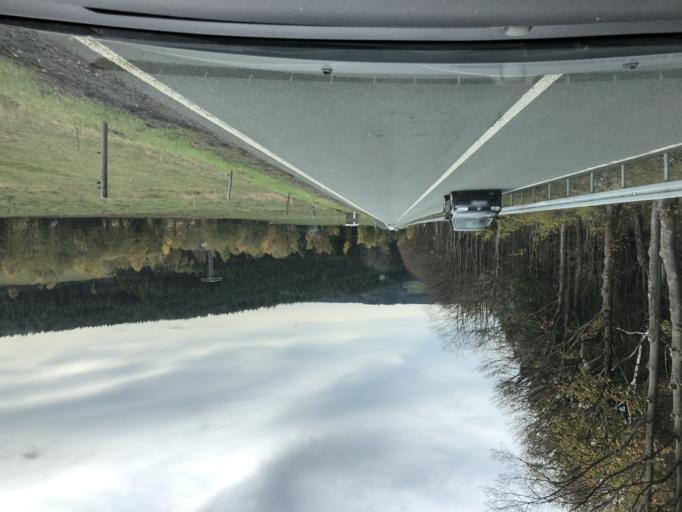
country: DE
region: Thuringia
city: Neuhaus am Rennweg
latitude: 50.5237
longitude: 11.1502
